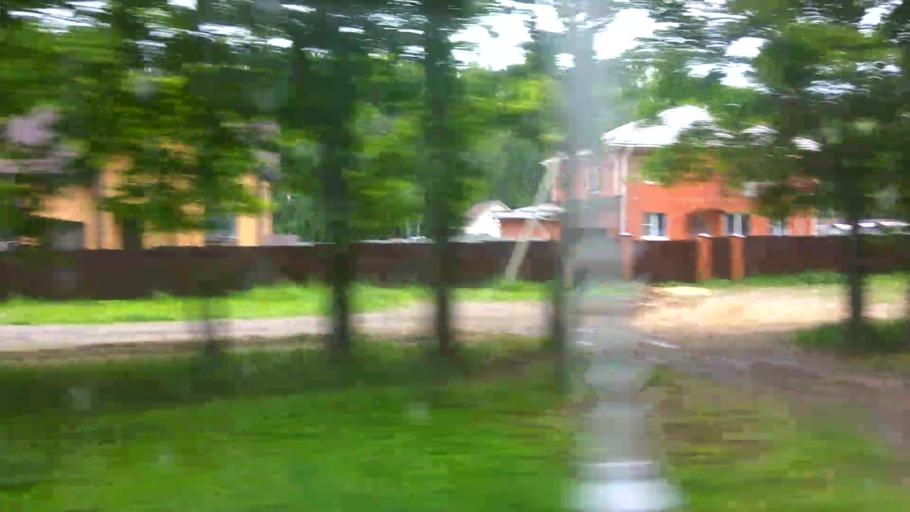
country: RU
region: Moskovskaya
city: Ozherel'ye
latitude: 54.8324
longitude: 38.2820
